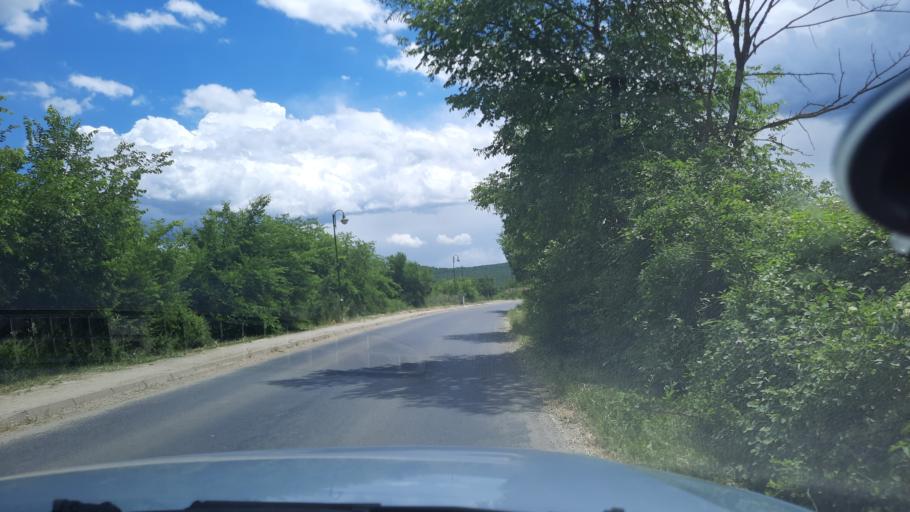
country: MK
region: Zelenikovo
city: Zelenikovo
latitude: 41.8819
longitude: 21.5954
